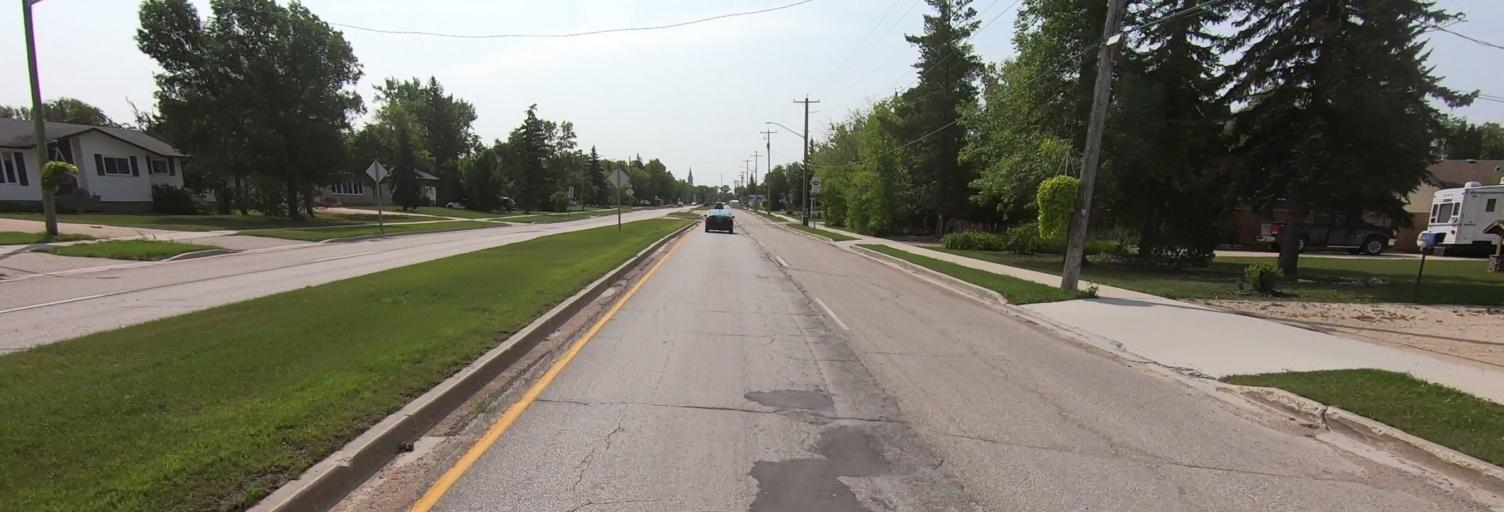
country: CA
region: Manitoba
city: Niverville
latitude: 49.6787
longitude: -97.1141
